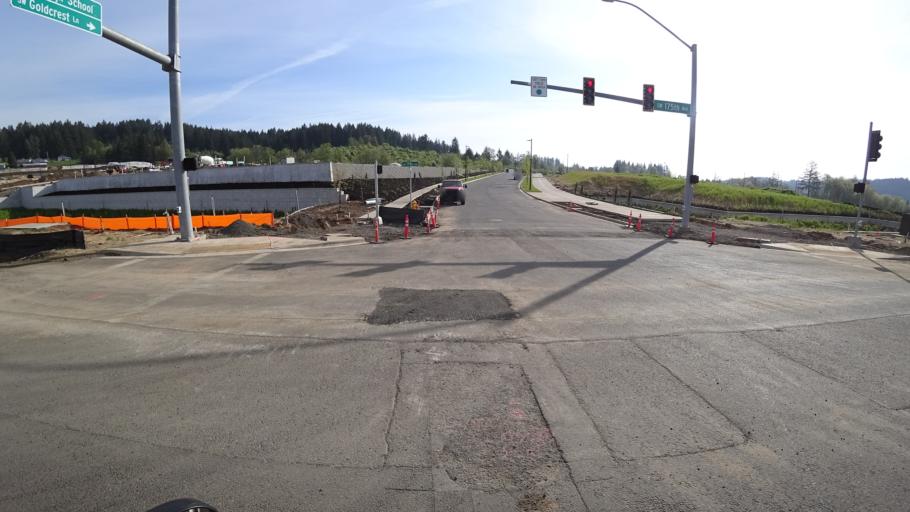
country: US
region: Oregon
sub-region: Washington County
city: King City
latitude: 45.4293
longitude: -122.8558
